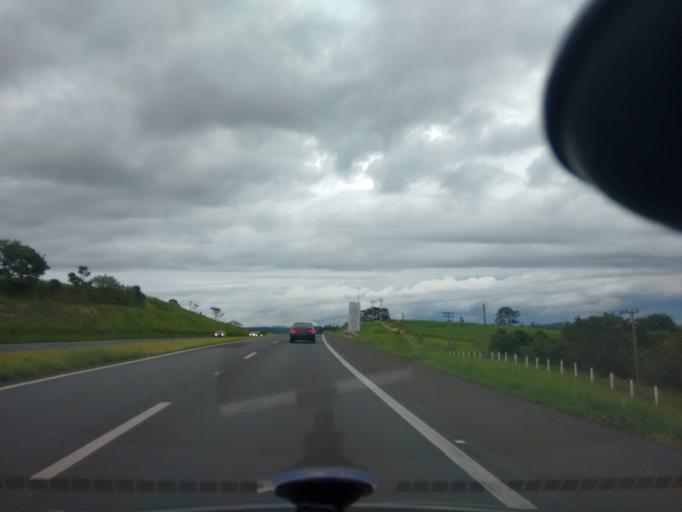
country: BR
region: Sao Paulo
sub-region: Rio Claro
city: Rio Claro
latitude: -22.3441
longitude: -47.6514
